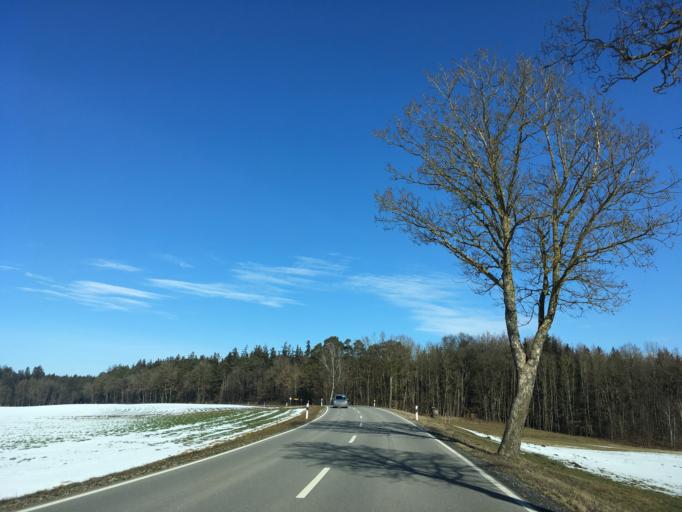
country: DE
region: Bavaria
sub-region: Upper Bavaria
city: Edling
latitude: 48.0786
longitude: 12.1612
